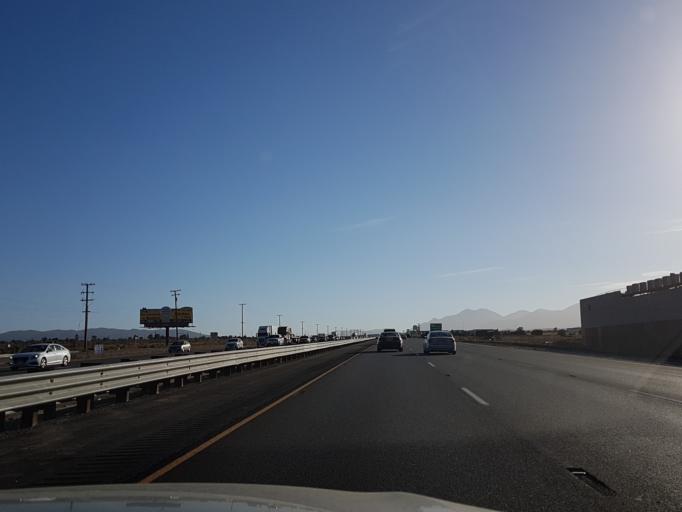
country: US
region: California
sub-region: San Bernardino County
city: Oak Hills
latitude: 34.4218
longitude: -117.3844
